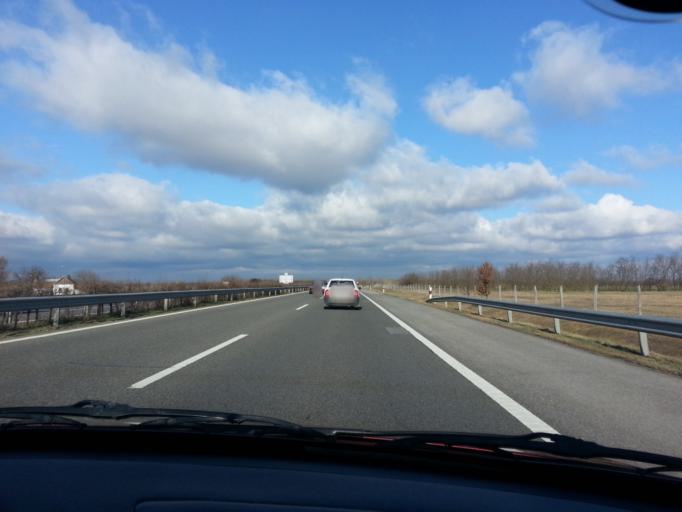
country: HU
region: Csongrad
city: Kistelek
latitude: 46.4742
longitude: 19.9243
